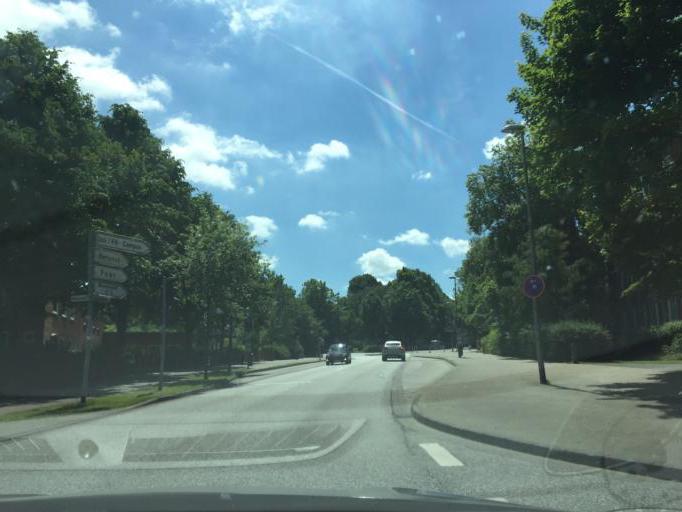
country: DE
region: Schleswig-Holstein
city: Flensburg
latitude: 54.7784
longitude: 9.4384
